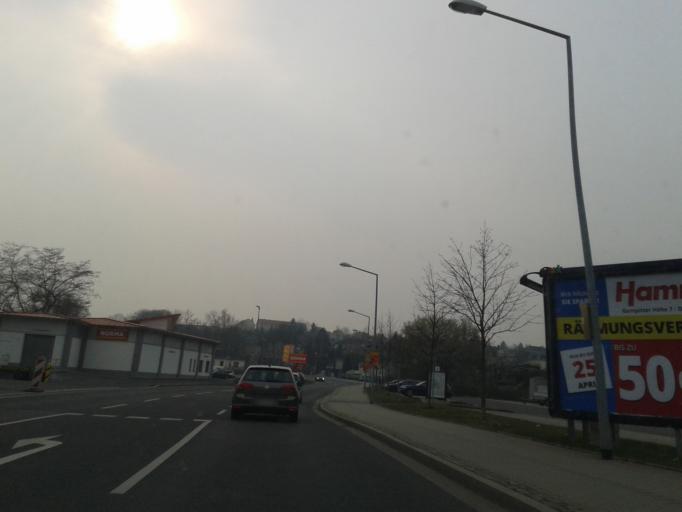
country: DE
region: Saxony
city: Freital
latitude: 51.0158
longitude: 13.6650
